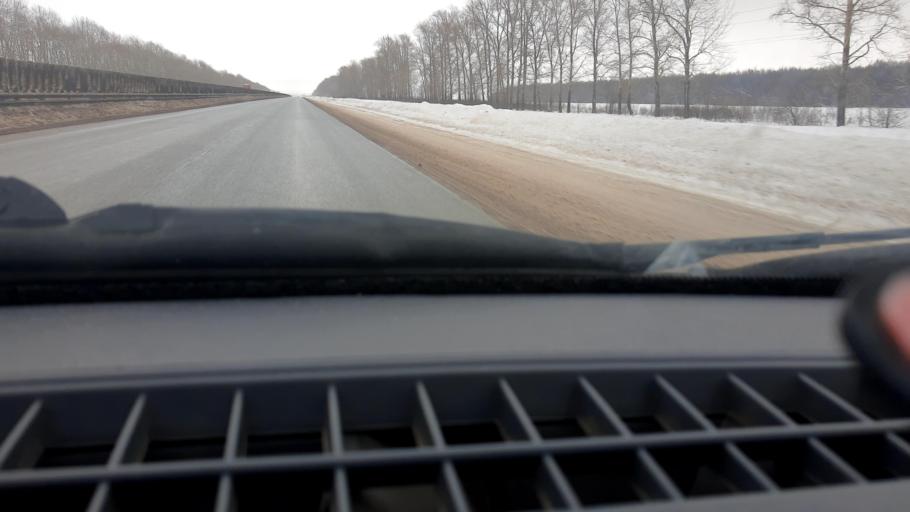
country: RU
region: Bashkortostan
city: Kushnarenkovo
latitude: 55.0457
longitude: 55.4464
